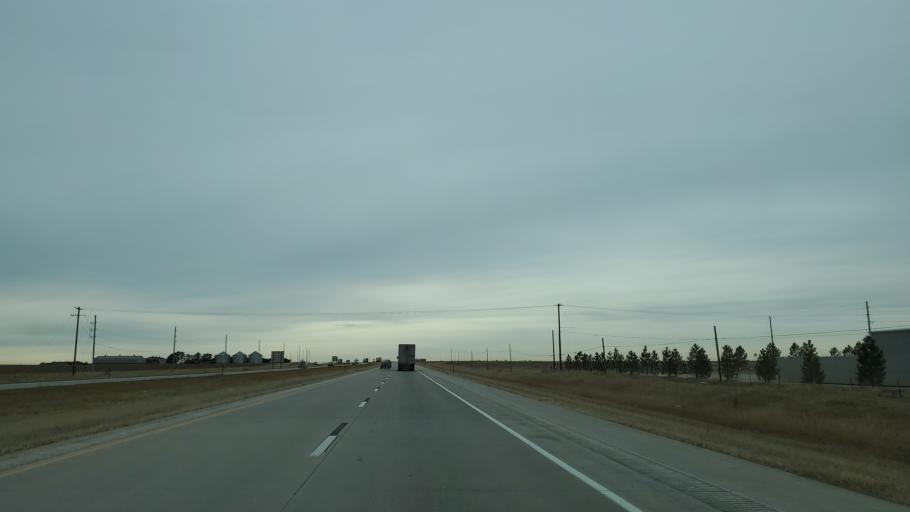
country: US
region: Colorado
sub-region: Adams County
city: Bennett
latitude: 39.7404
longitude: -104.6199
